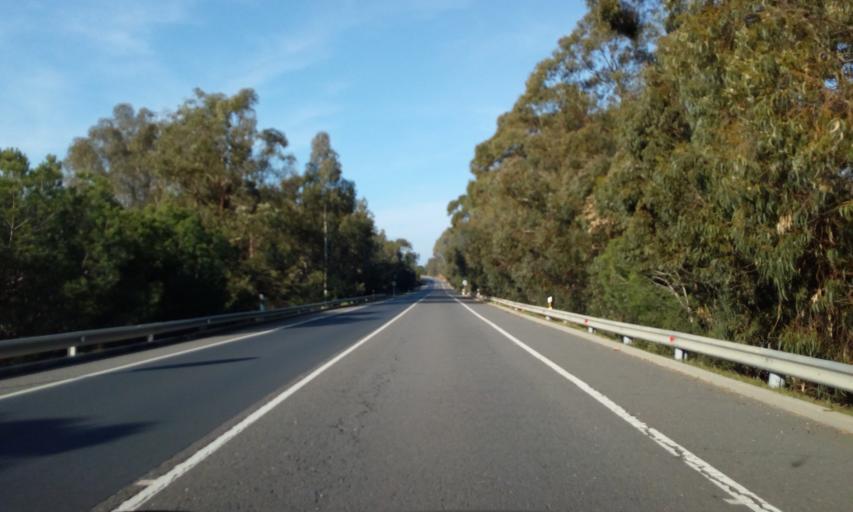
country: ES
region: Andalusia
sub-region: Provincia de Huelva
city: Isla Cristina
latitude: 37.2465
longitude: -7.2802
